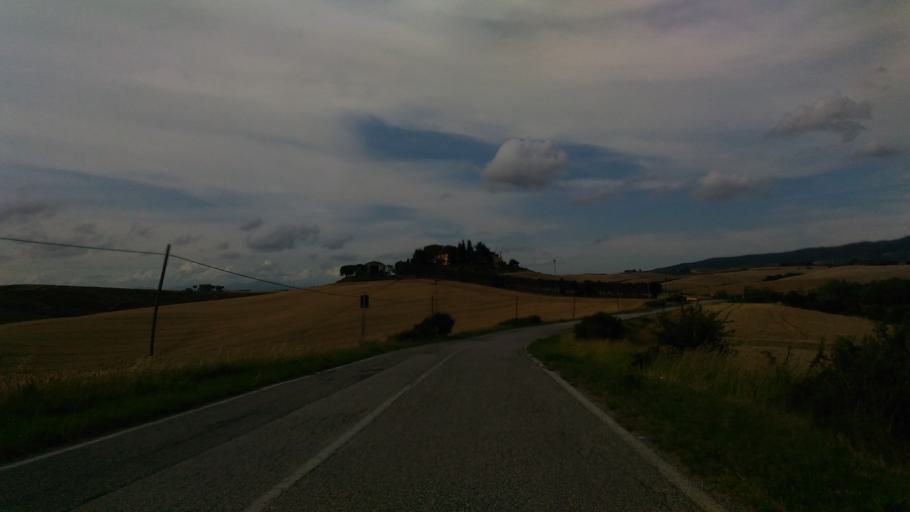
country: IT
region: Tuscany
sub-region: Province of Pisa
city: Orciano Pisano
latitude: 43.4489
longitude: 10.5118
